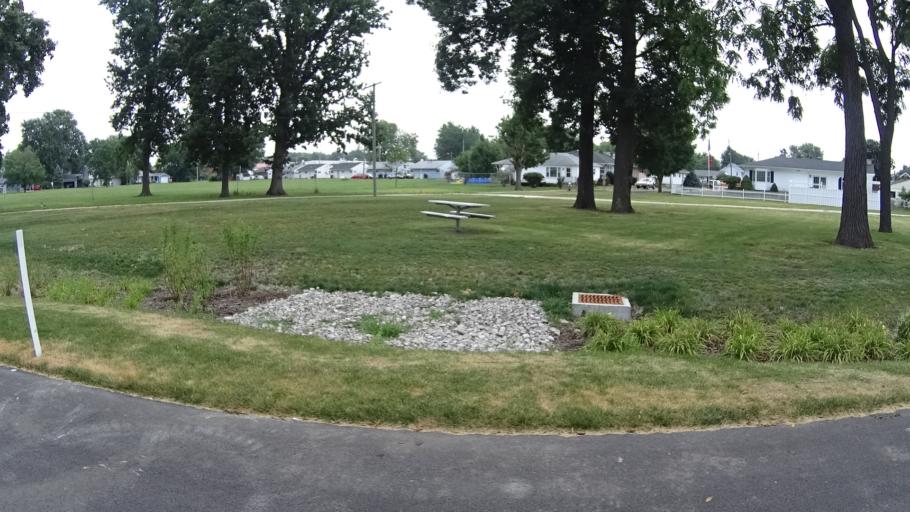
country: US
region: Ohio
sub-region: Erie County
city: Sandusky
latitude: 41.4472
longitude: -82.7461
